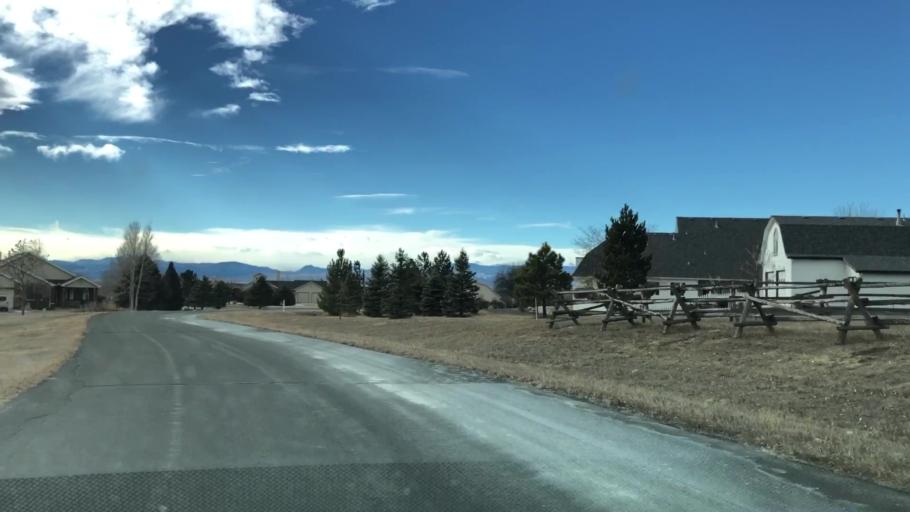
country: US
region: Colorado
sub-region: Weld County
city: Windsor
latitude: 40.5328
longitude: -104.9328
